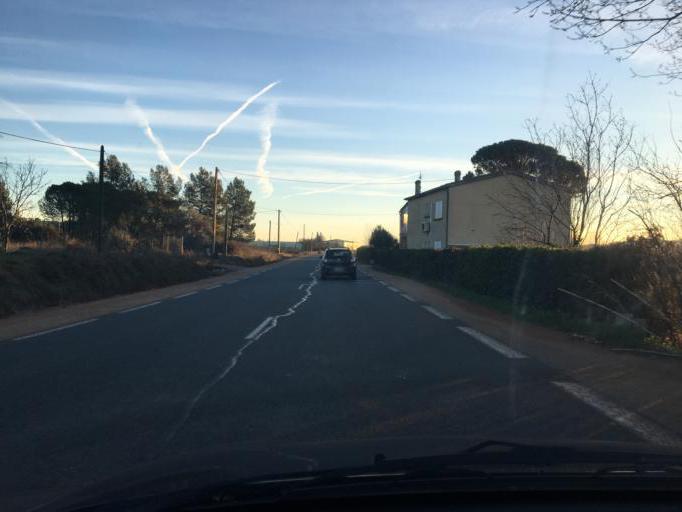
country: FR
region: Provence-Alpes-Cote d'Azur
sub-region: Departement du Var
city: Les Arcs
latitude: 43.4502
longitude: 6.4570
